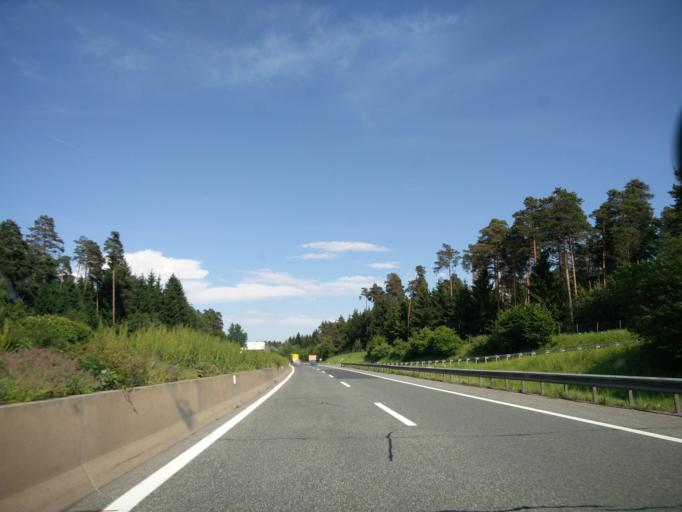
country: AT
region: Carinthia
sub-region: Politischer Bezirk Klagenfurt Land
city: Poggersdorf
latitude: 46.6378
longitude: 14.4507
